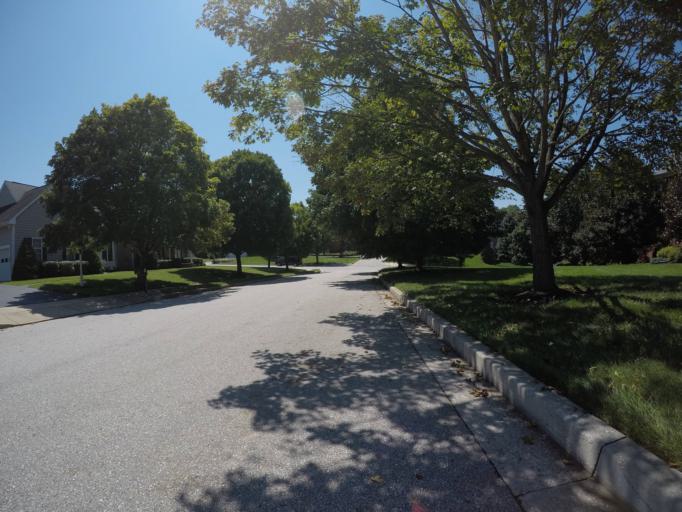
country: US
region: Maryland
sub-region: Howard County
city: Columbia
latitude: 39.2914
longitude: -76.8853
